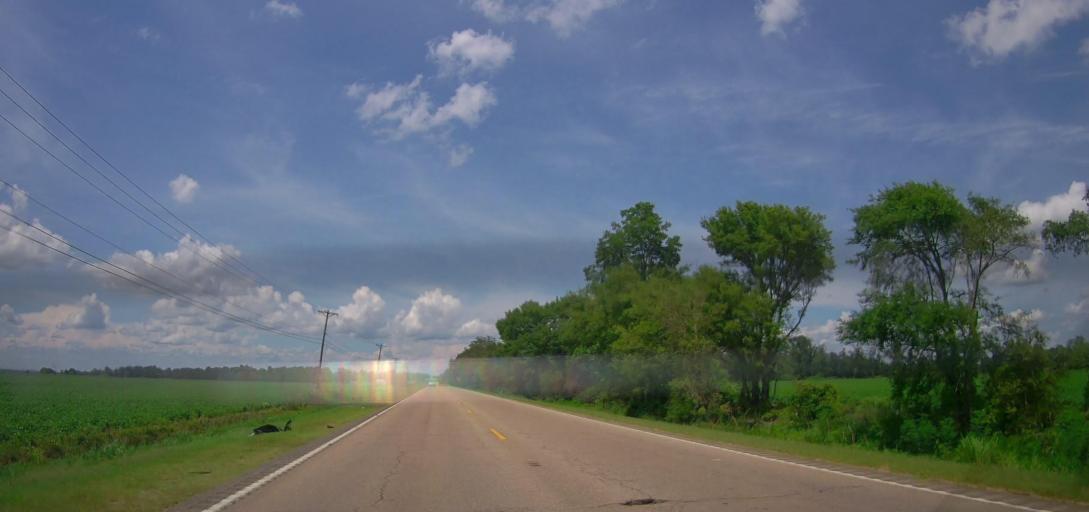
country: US
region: Mississippi
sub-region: Lee County
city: Shannon
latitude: 34.1442
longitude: -88.7194
